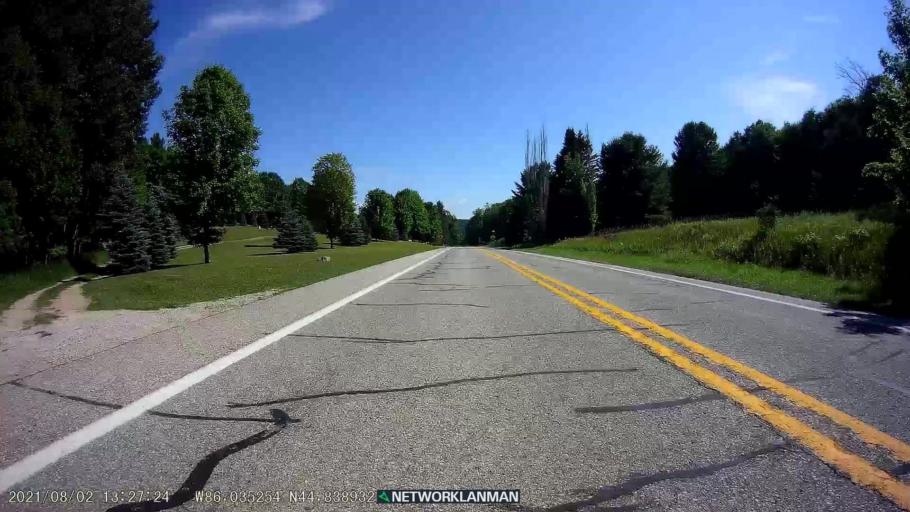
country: US
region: Michigan
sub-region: Benzie County
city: Beulah
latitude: 44.8391
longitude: -86.0353
